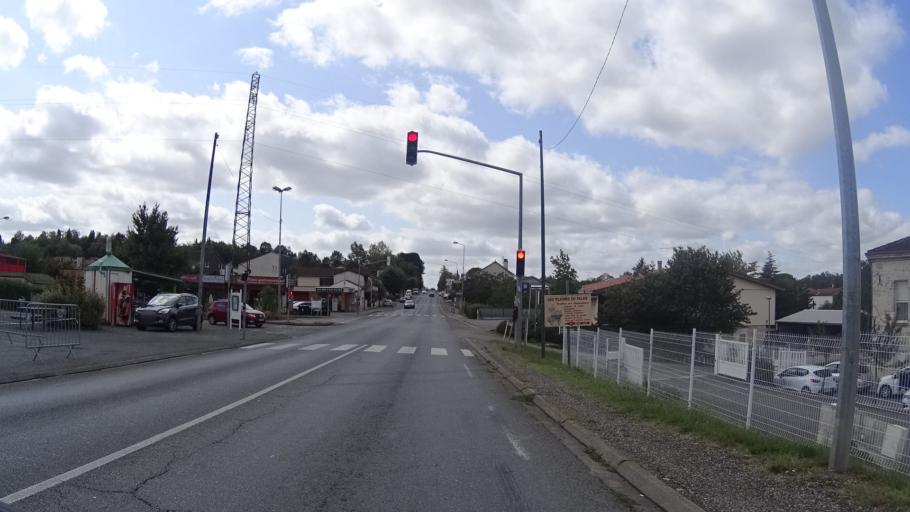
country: FR
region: Aquitaine
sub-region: Departement du Lot-et-Garonne
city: Foulayronnes
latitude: 44.2388
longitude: 0.6441
